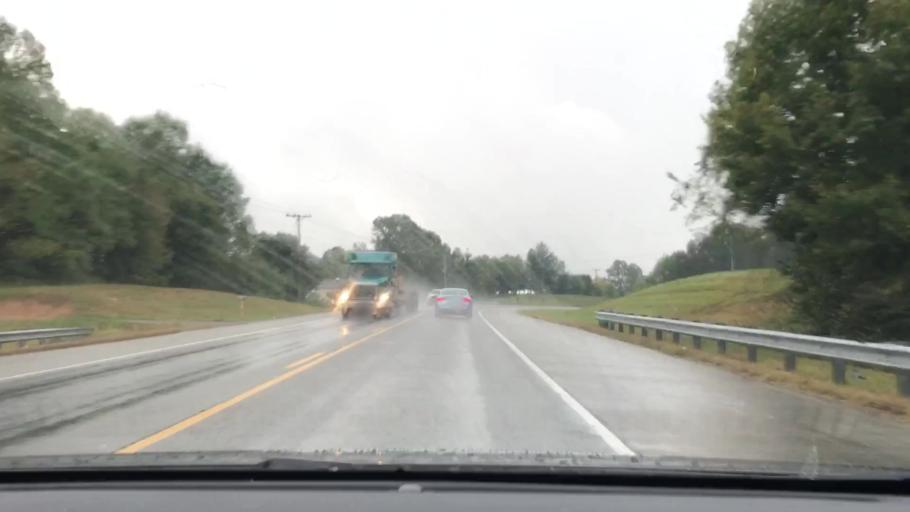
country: US
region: Tennessee
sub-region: Sumner County
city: Westmoreland
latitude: 36.5295
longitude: -86.1802
